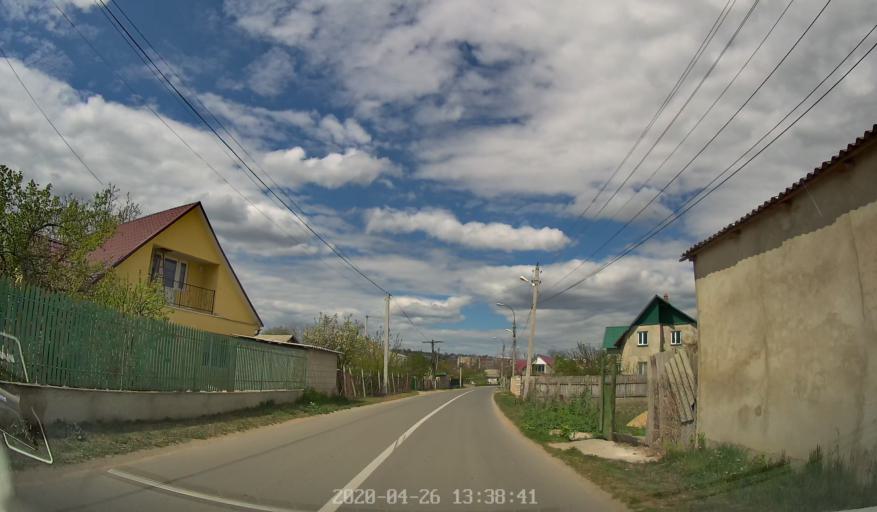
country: MD
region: Criuleni
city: Criuleni
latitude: 47.2096
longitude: 29.1655
